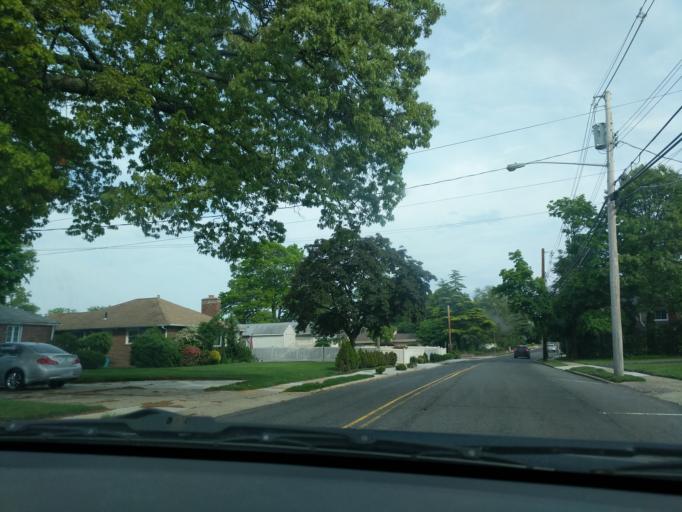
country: US
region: New York
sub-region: Nassau County
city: Rockville Centre
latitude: 40.6491
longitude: -73.6397
